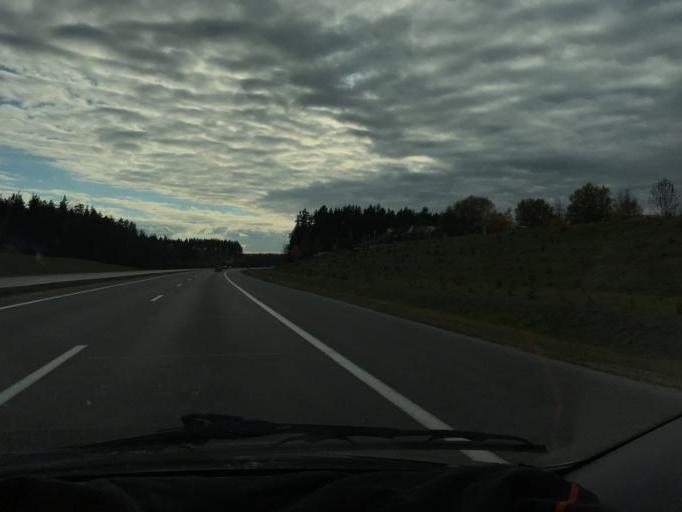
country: BY
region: Minsk
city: Astrashytski Haradok
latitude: 54.0443
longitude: 27.6999
